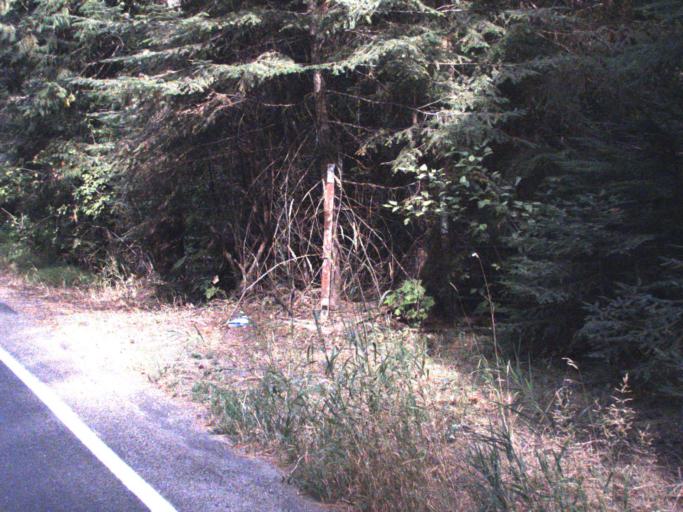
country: US
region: Washington
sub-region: Spokane County
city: Trentwood
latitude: 47.8515
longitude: -117.1653
